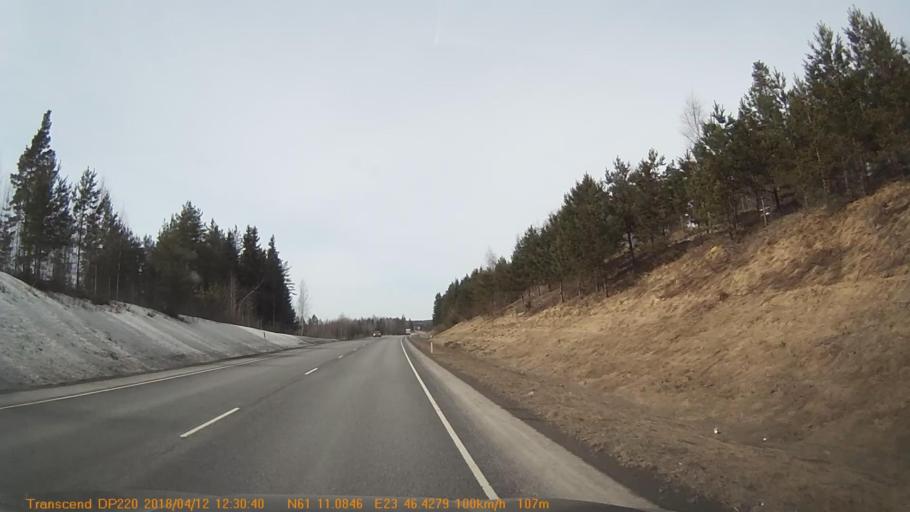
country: FI
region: Pirkanmaa
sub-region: Etelae-Pirkanmaa
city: Viiala
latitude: 61.1849
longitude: 23.7728
